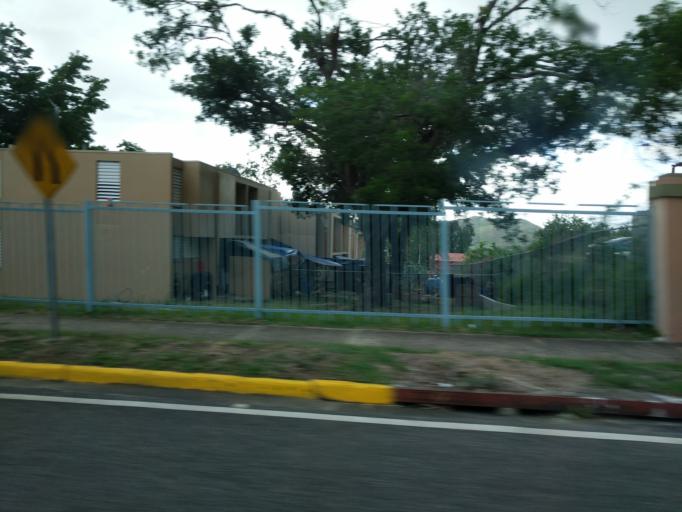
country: PR
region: Coamo
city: Coamo
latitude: 18.0765
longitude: -66.3678
